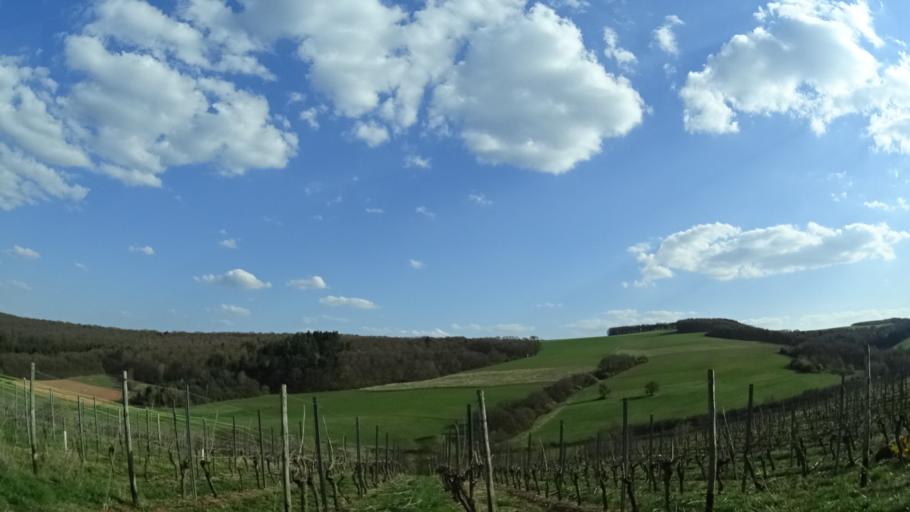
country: DE
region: Rheinland-Pfalz
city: Kirschroth
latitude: 49.7582
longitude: 7.5746
